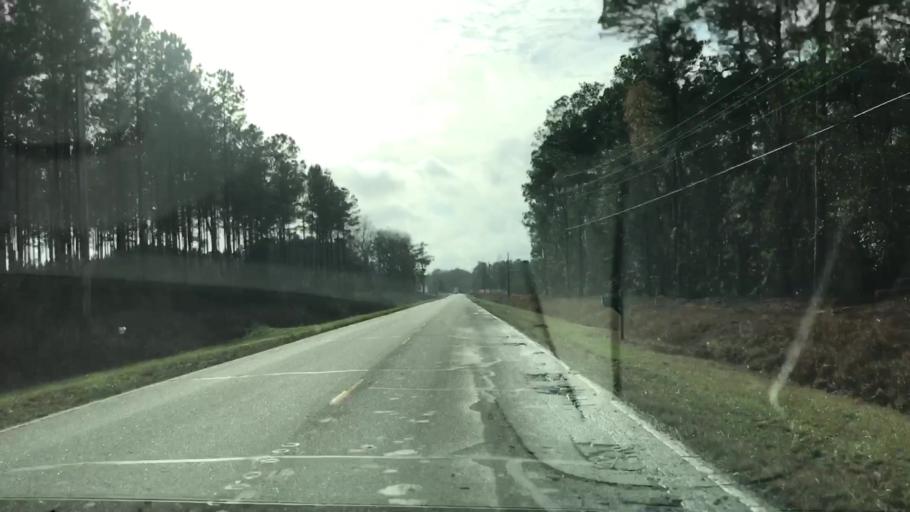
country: US
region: South Carolina
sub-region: Williamsburg County
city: Andrews
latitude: 33.3641
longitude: -79.6479
